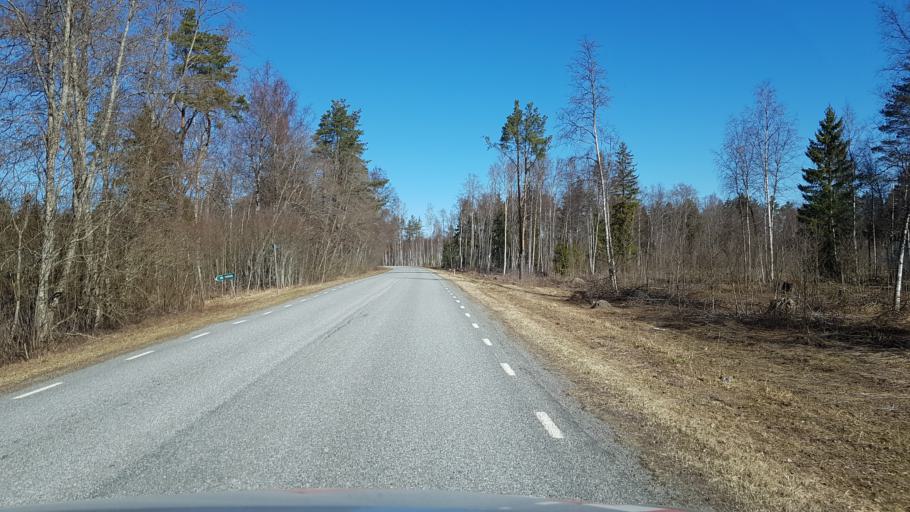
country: EE
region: Laeaene-Virumaa
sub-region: Haljala vald
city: Haljala
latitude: 59.4825
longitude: 26.2482
